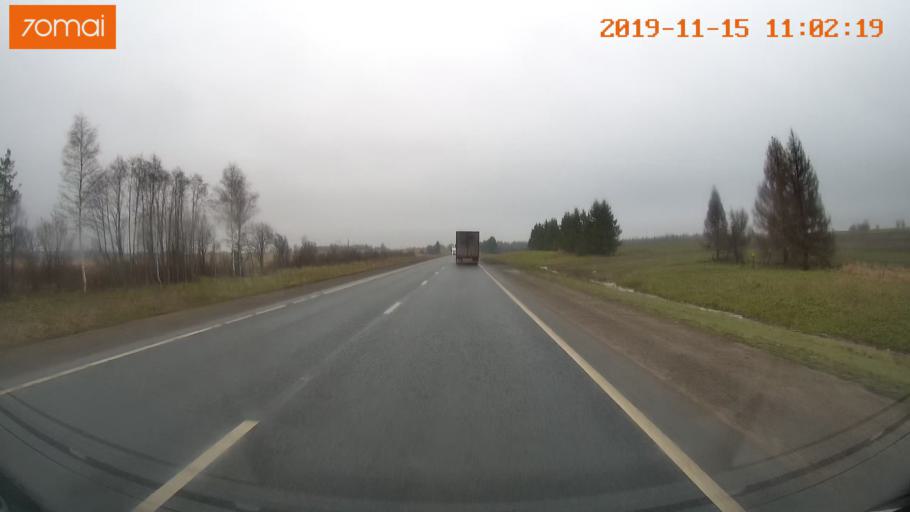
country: RU
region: Vologda
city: Chebsara
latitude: 59.1293
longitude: 38.9382
